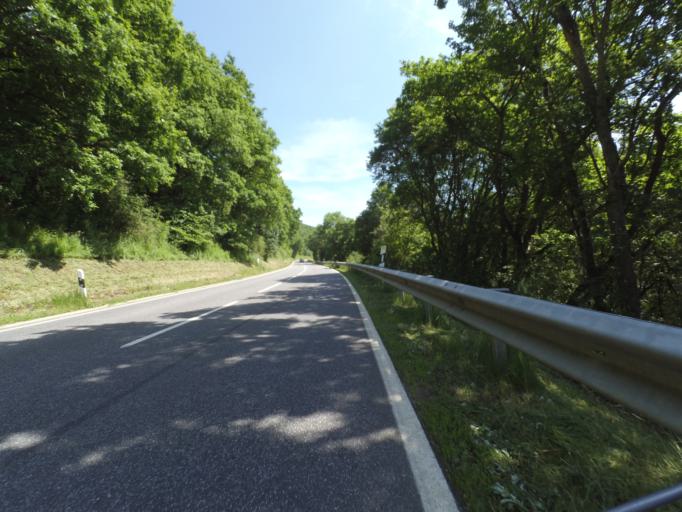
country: DE
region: Rheinland-Pfalz
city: Monreal
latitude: 50.3061
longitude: 7.1718
